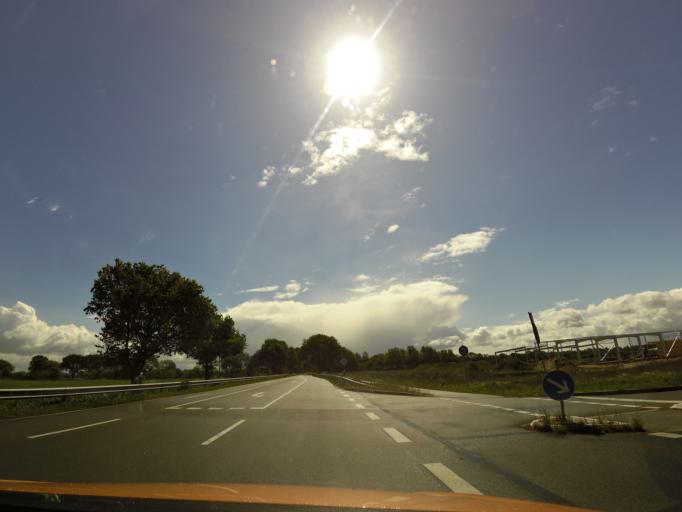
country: DE
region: Lower Saxony
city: Oldenburg
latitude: 53.1318
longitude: 8.2916
